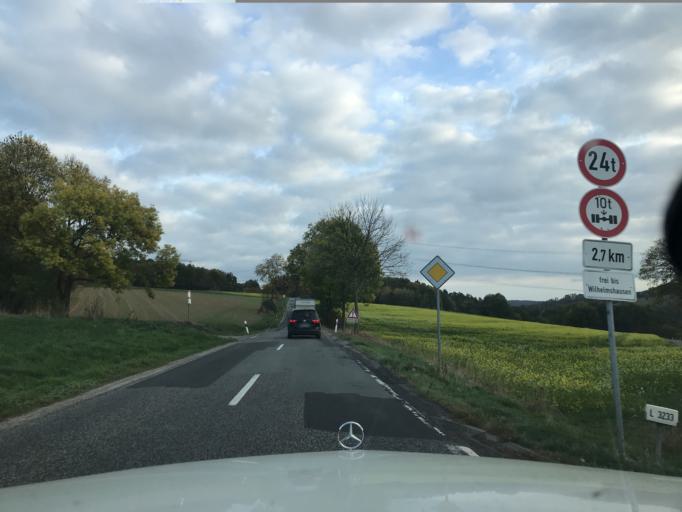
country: DE
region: Hesse
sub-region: Regierungsbezirk Kassel
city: Fuldatal
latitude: 51.4072
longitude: 9.5514
